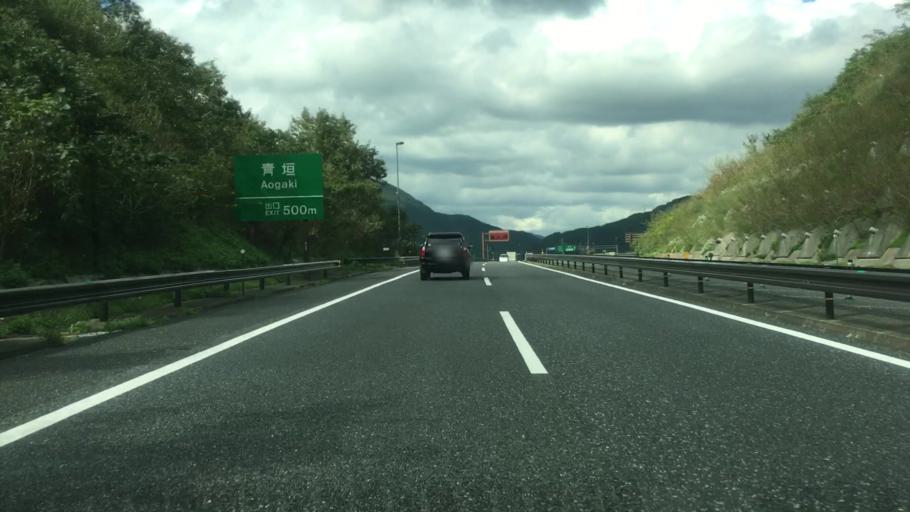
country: JP
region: Kyoto
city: Fukuchiyama
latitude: 35.2377
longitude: 135.0164
